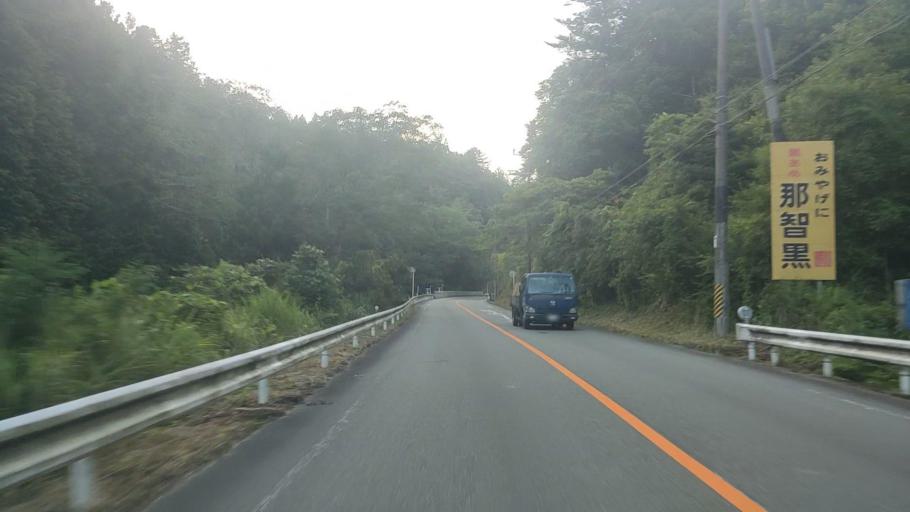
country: JP
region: Wakayama
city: Tanabe
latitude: 33.8148
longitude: 135.6161
